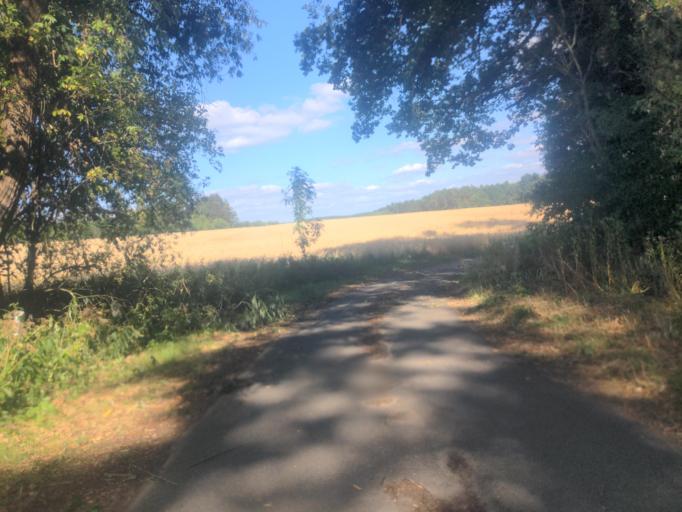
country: DE
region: Lower Saxony
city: Neu Darchau
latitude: 53.2085
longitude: 10.8604
